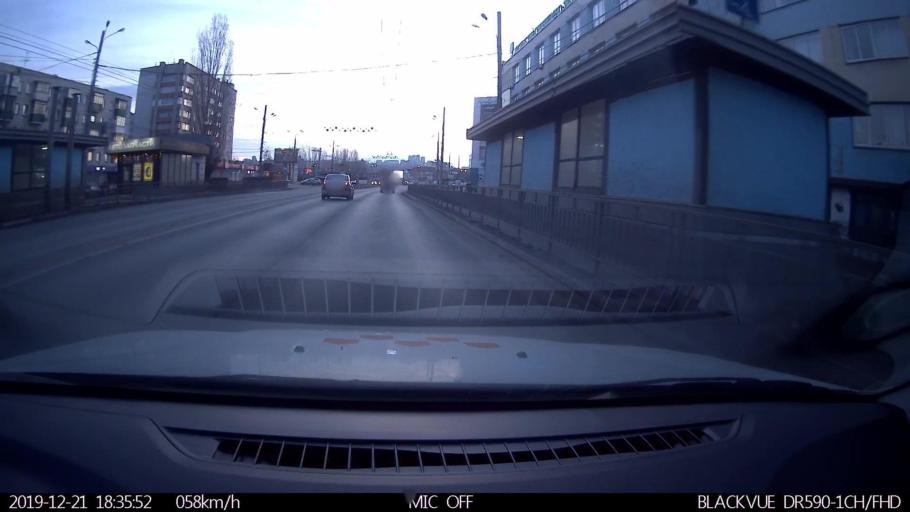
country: RU
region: Nizjnij Novgorod
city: Nizhniy Novgorod
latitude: 56.3209
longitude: 43.9255
